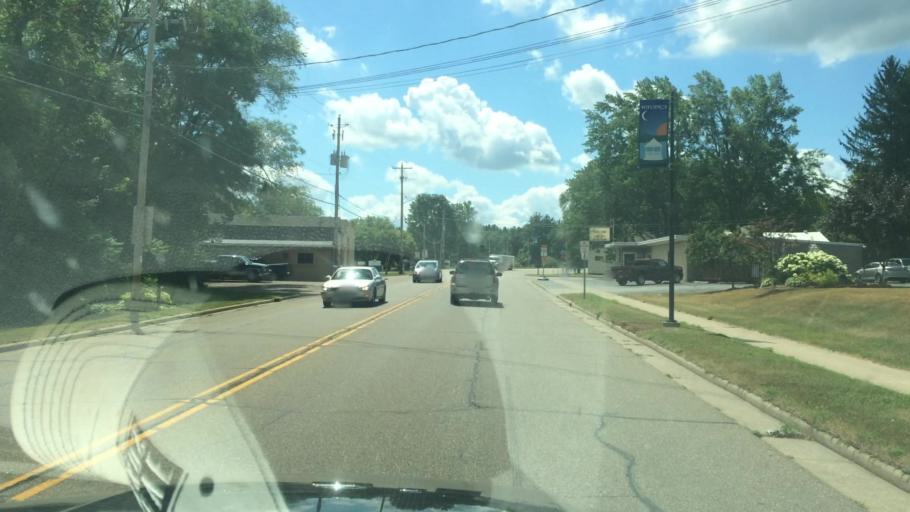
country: US
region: Wisconsin
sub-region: Waupaca County
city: Waupaca
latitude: 44.3430
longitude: -89.0699
